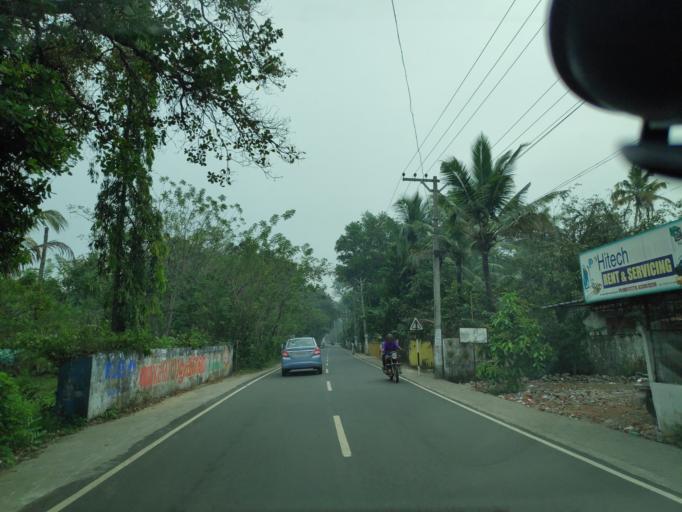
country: IN
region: Kerala
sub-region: Alappuzha
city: Shertallai
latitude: 9.6072
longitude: 76.3532
